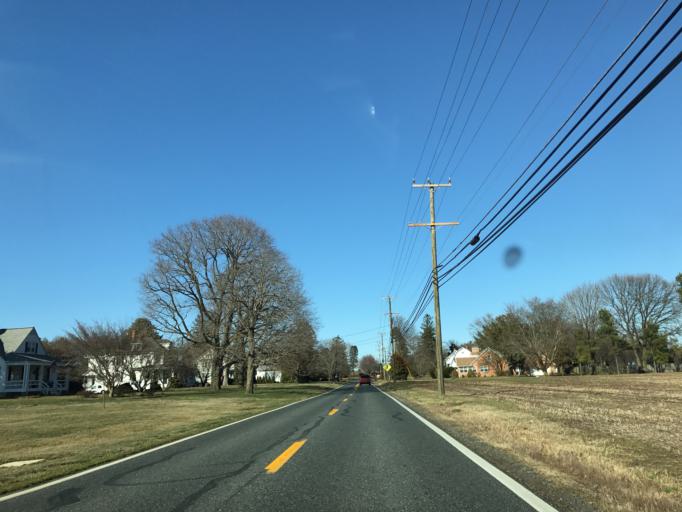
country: US
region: Maryland
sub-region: Harford County
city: Perryman
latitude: 39.4621
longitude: -76.2070
